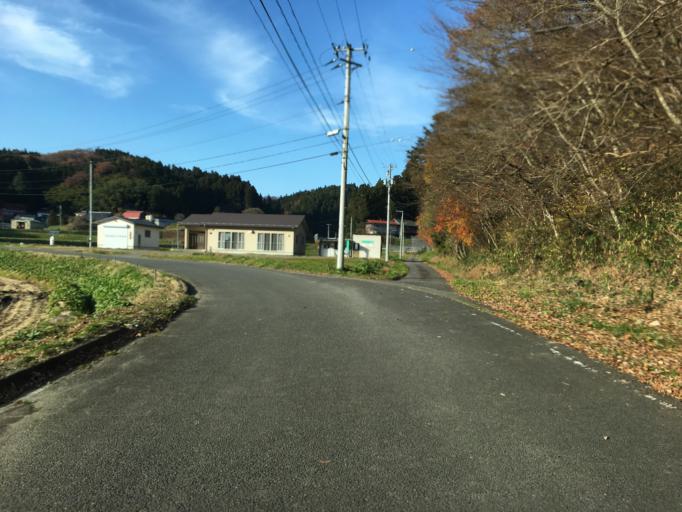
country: JP
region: Fukushima
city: Ishikawa
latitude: 37.2391
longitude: 140.5884
